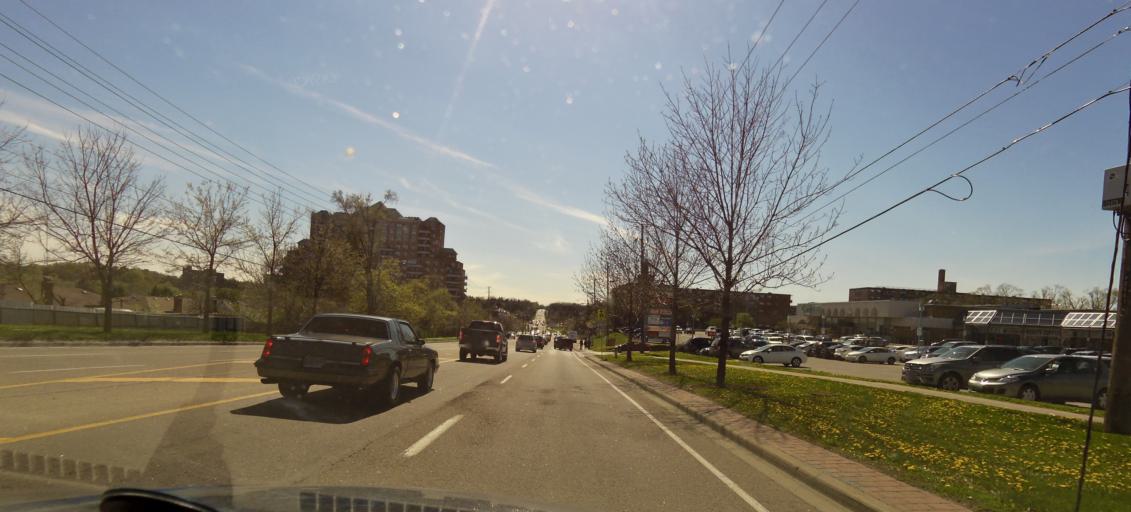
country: CA
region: Ontario
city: Concord
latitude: 43.7483
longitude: -79.5601
